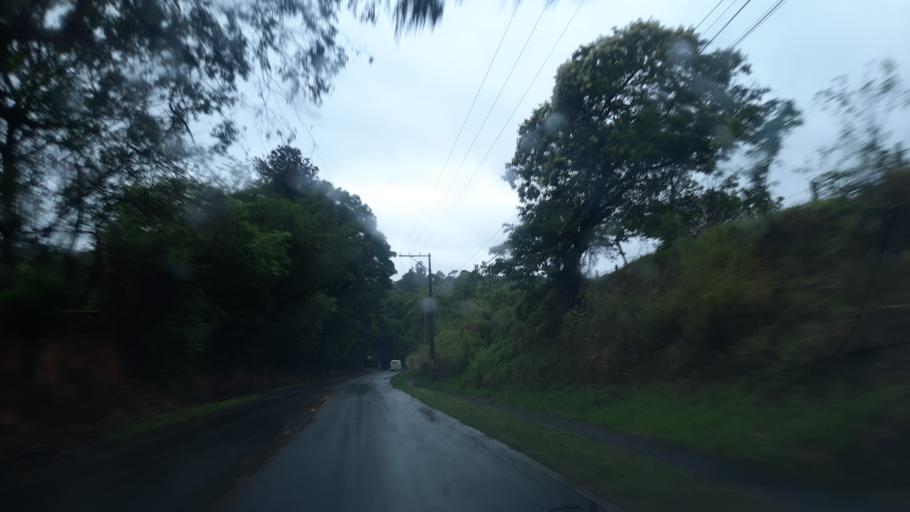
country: BR
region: Sao Paulo
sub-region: Atibaia
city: Atibaia
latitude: -23.0860
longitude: -46.5306
